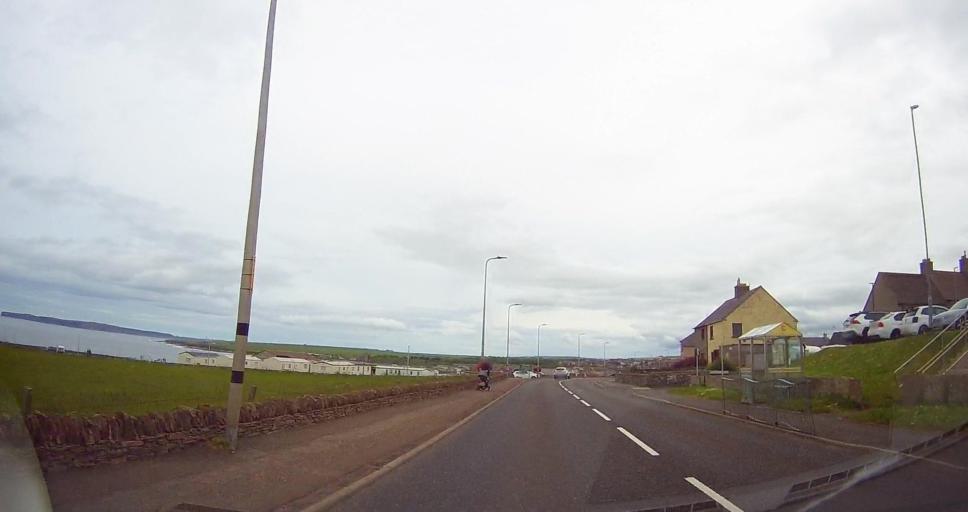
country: GB
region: Scotland
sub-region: Highland
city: Thurso
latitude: 58.5980
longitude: -3.5318
